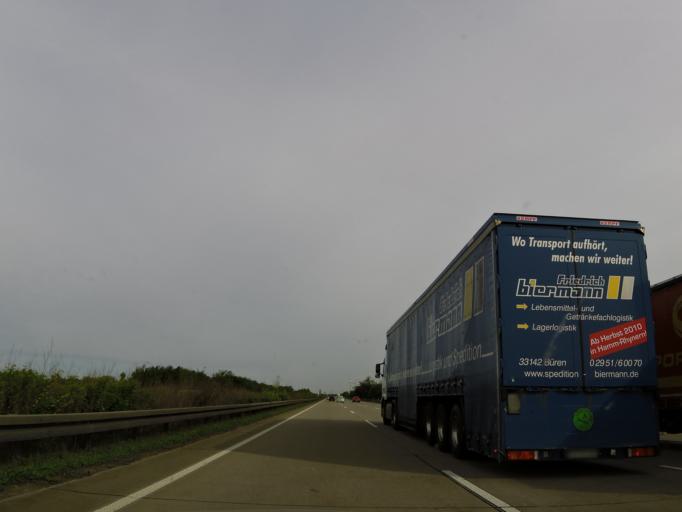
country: DE
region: Lower Saxony
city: Algermissen
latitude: 52.2457
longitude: 9.9257
